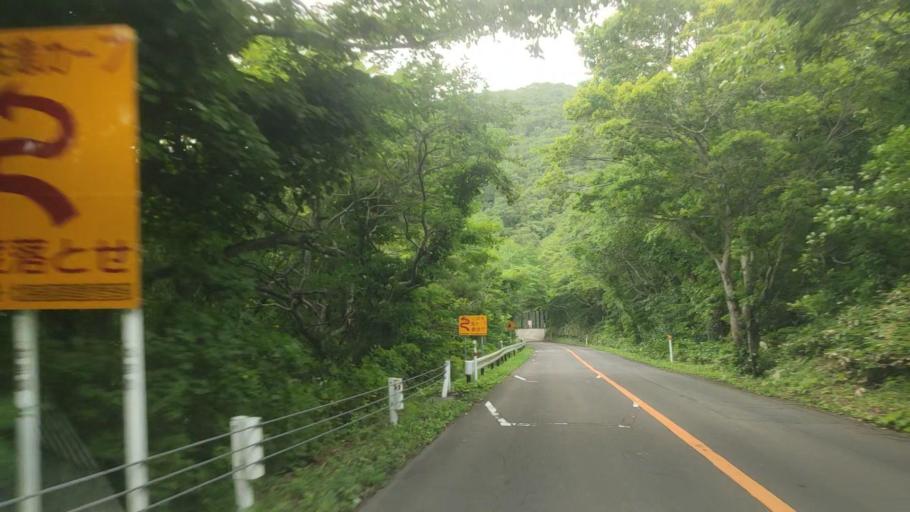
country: JP
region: Hokkaido
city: Hakodate
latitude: 41.7624
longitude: 140.7008
